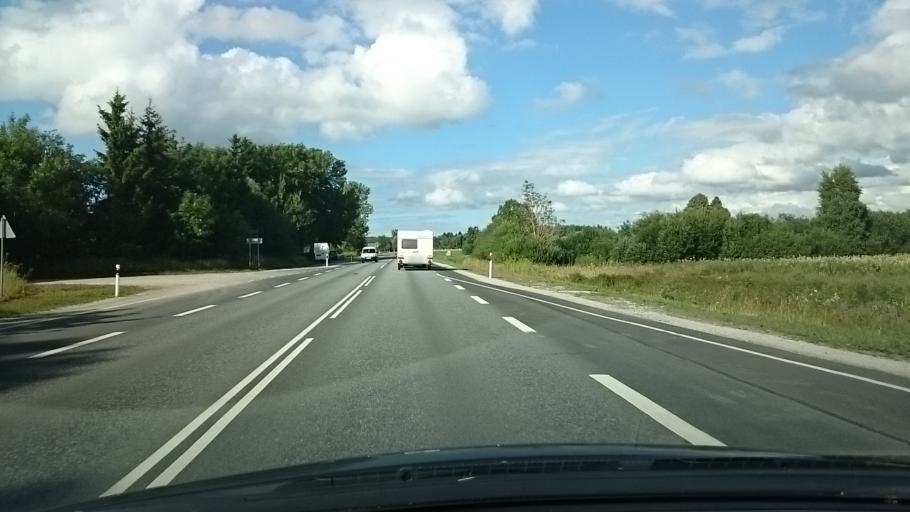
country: EE
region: Harju
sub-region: Keila linn
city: Keila
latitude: 59.2948
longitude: 24.3428
